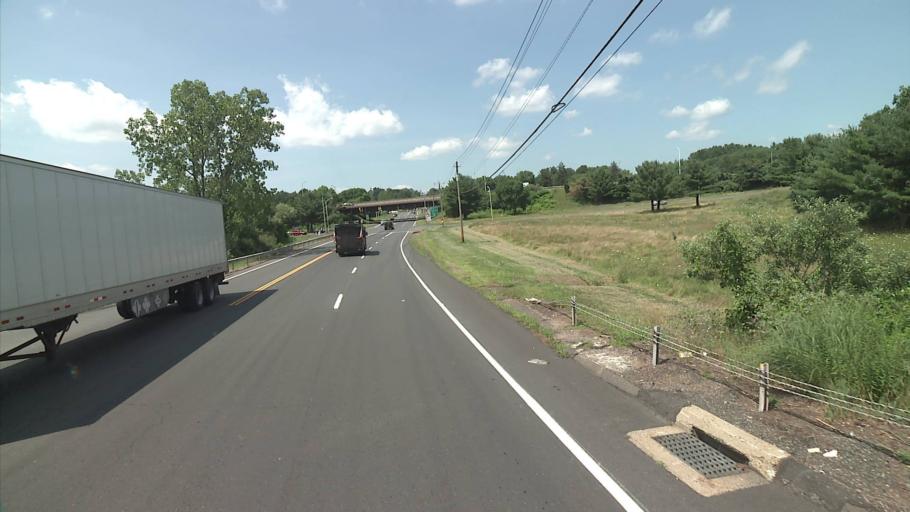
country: US
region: Connecticut
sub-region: Tolland County
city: Rockville
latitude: 41.8530
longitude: -72.4281
